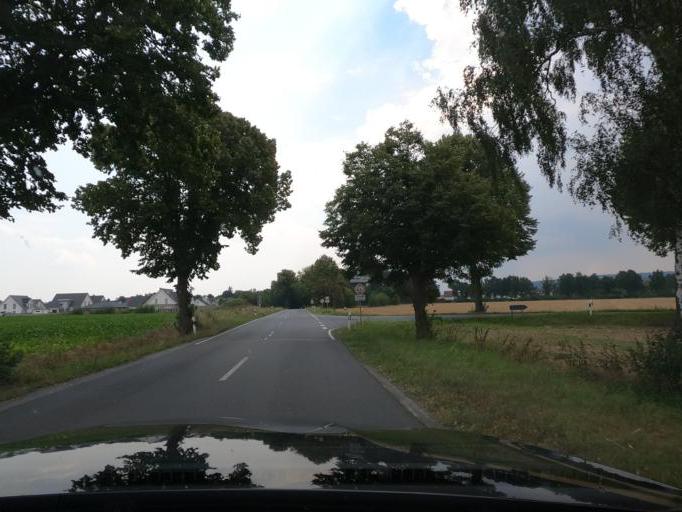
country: DE
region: Lower Saxony
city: Alt Wallmoden
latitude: 52.0396
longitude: 10.2989
